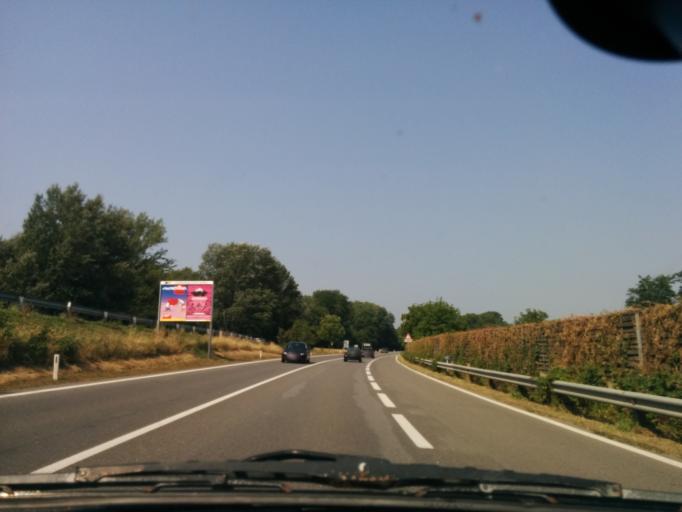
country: AT
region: Lower Austria
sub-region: Politischer Bezirk Krems
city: Grafenegg
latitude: 48.4082
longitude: 15.7229
